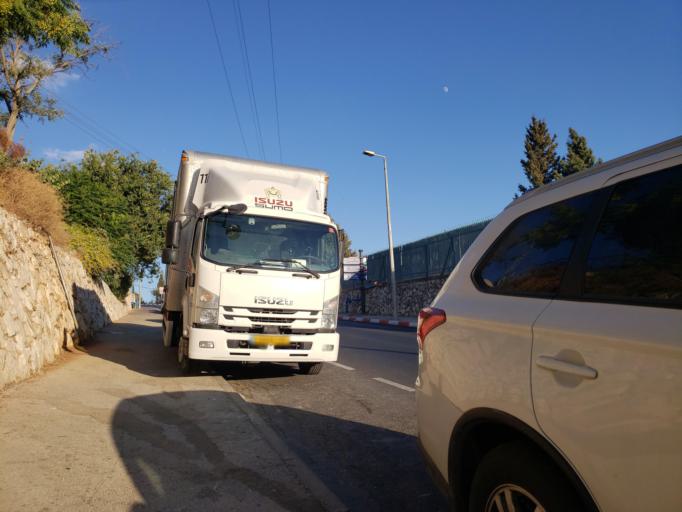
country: IL
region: Northern District
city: Safed
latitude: 32.9572
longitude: 35.4941
